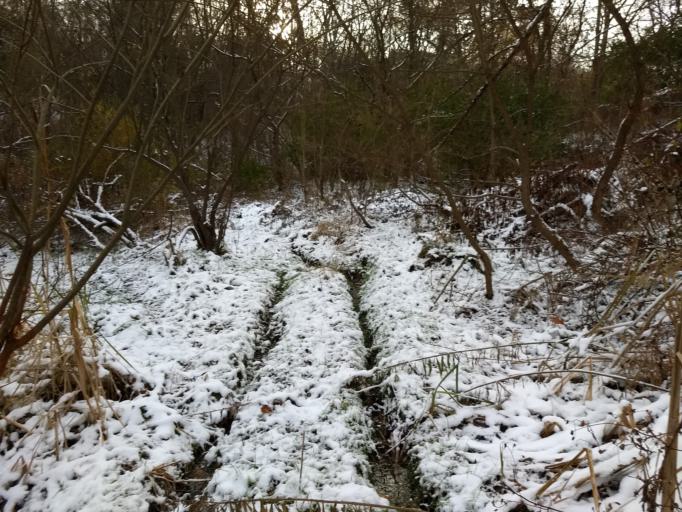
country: US
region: Pennsylvania
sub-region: Allegheny County
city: Mount Oliver
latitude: 40.4053
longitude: -80.0055
